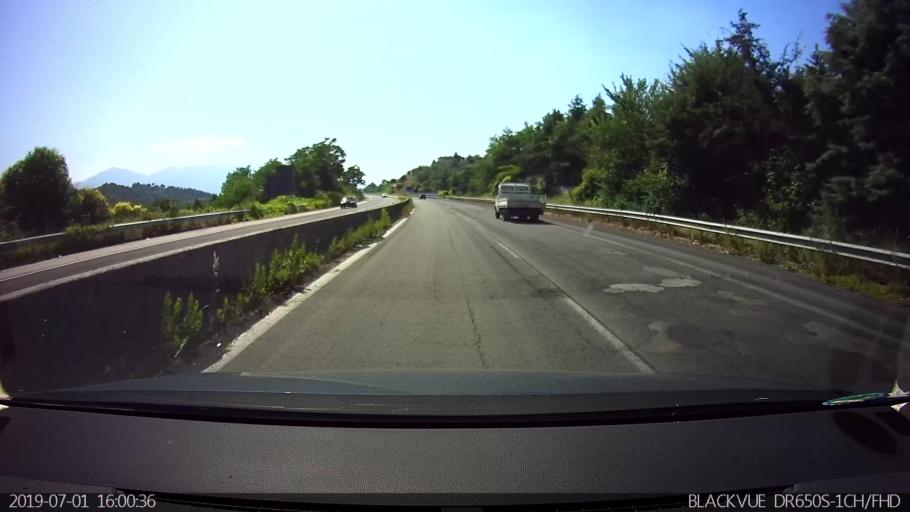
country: IT
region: Latium
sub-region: Provincia di Frosinone
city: Castelmassimo
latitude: 41.6639
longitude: 13.3930
